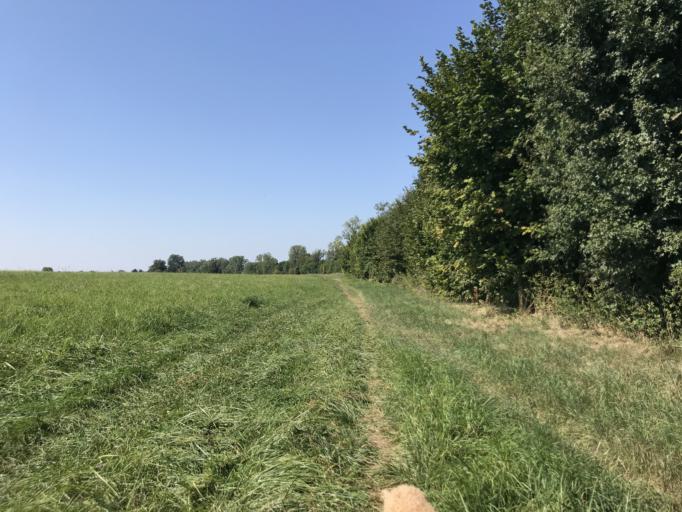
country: DE
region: Hesse
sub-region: Regierungsbezirk Darmstadt
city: Bischofsheim
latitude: 50.0013
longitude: 8.3695
